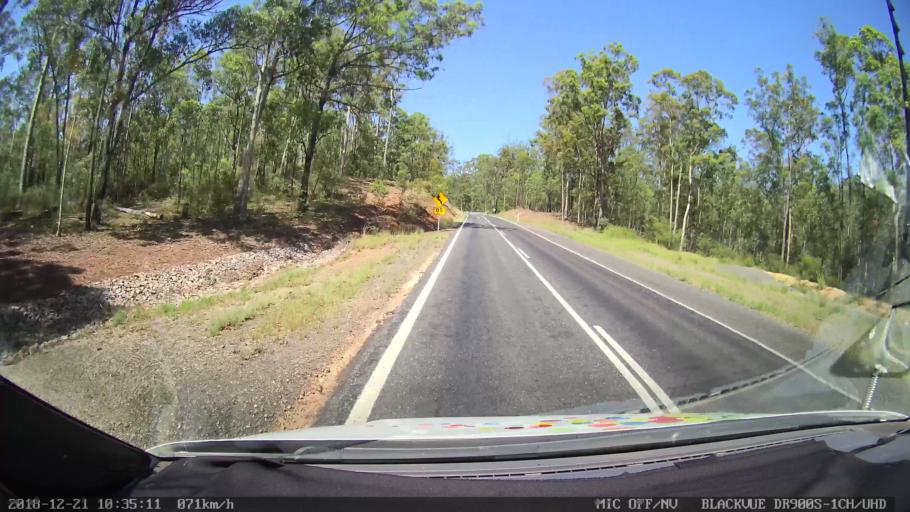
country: AU
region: New South Wales
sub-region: Clarence Valley
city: South Grafton
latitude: -29.6179
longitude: 152.6465
